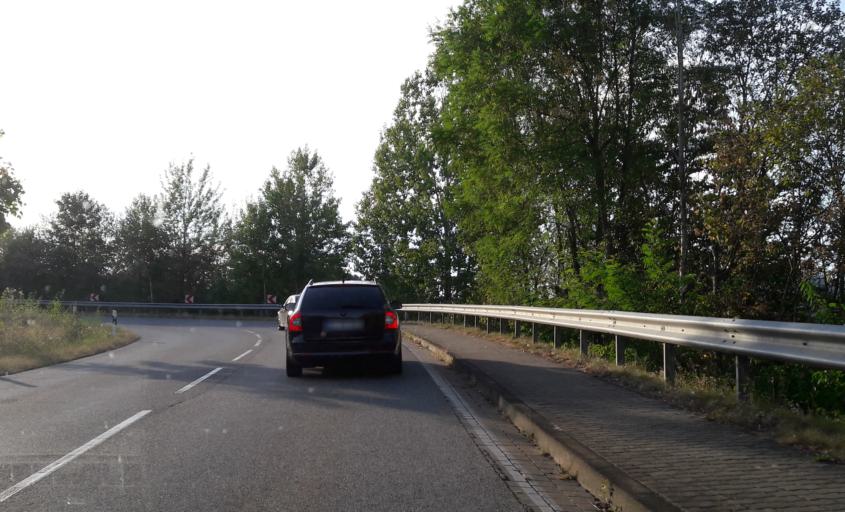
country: DE
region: Rheinland-Pfalz
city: Briedel
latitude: 50.0403
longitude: 7.1476
